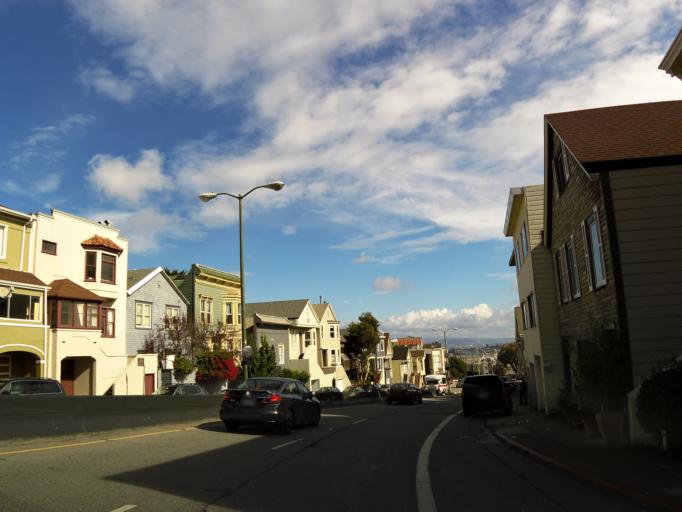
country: US
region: California
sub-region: San Francisco County
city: San Francisco
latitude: 37.7610
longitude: -122.4427
